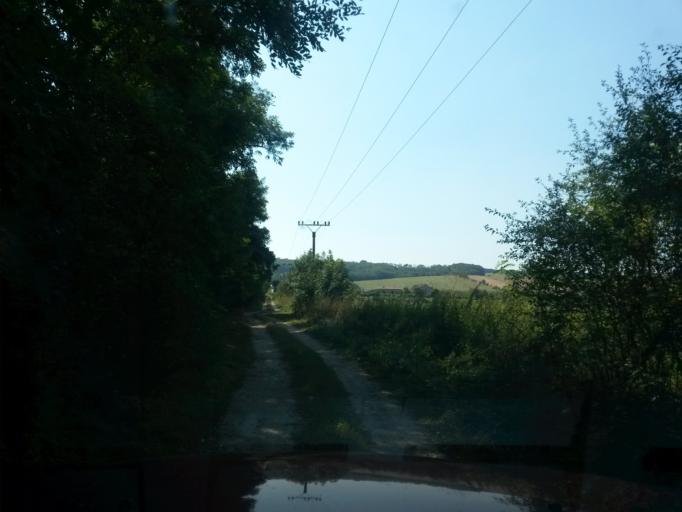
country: HU
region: Borsod-Abauj-Zemplen
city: Gonc
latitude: 48.5359
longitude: 21.1569
